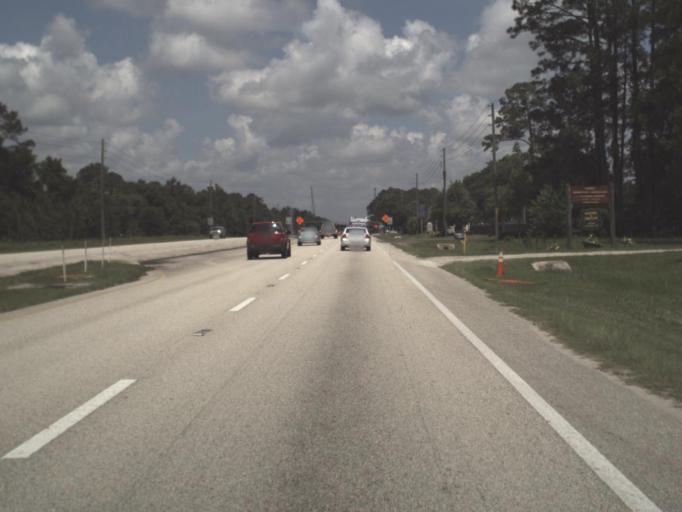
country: US
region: Florida
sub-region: Saint Johns County
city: Palm Valley
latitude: 30.0844
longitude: -81.4582
